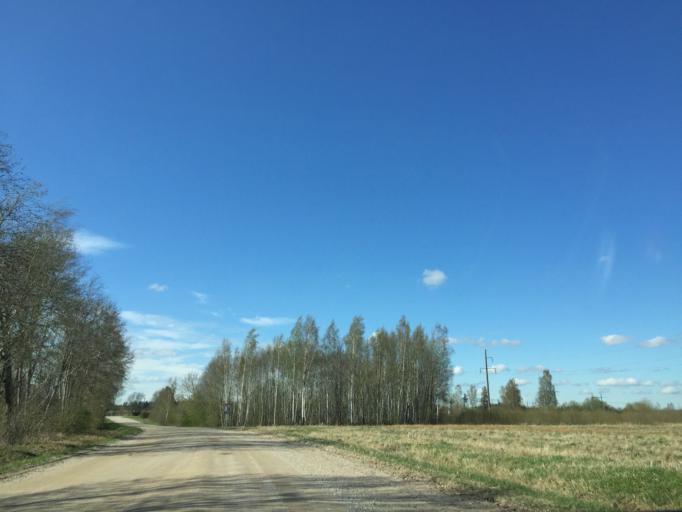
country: EE
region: Valgamaa
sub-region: Valga linn
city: Valga
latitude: 57.8534
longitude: 26.1700
